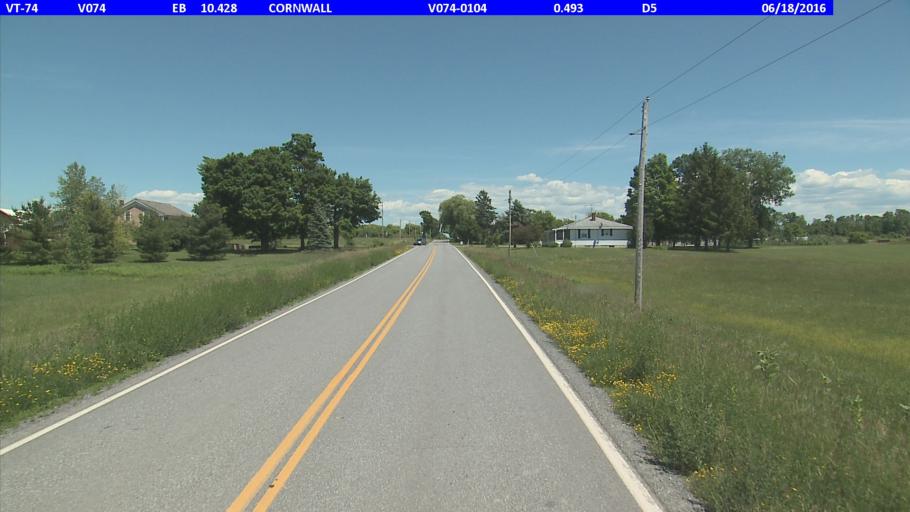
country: US
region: Vermont
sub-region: Addison County
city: Middlebury (village)
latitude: 43.9425
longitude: -73.2479
